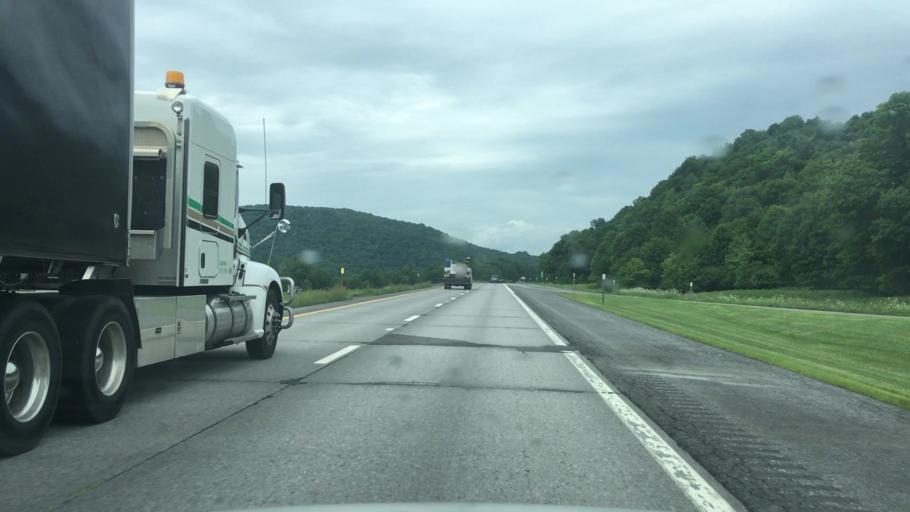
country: US
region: New York
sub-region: Otsego County
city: Worcester
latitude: 42.5751
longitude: -74.7664
